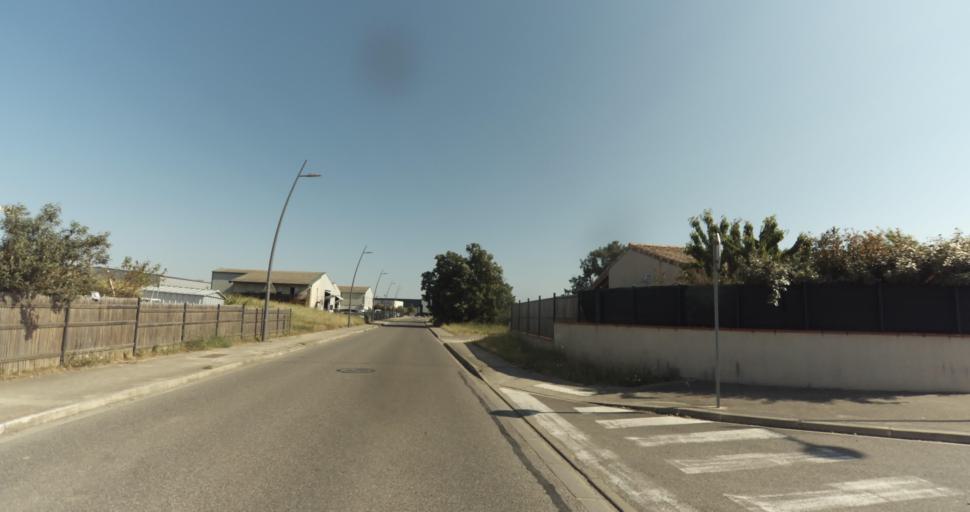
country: FR
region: Midi-Pyrenees
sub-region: Departement de la Haute-Garonne
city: Tournefeuille
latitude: 43.5899
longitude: 1.2989
